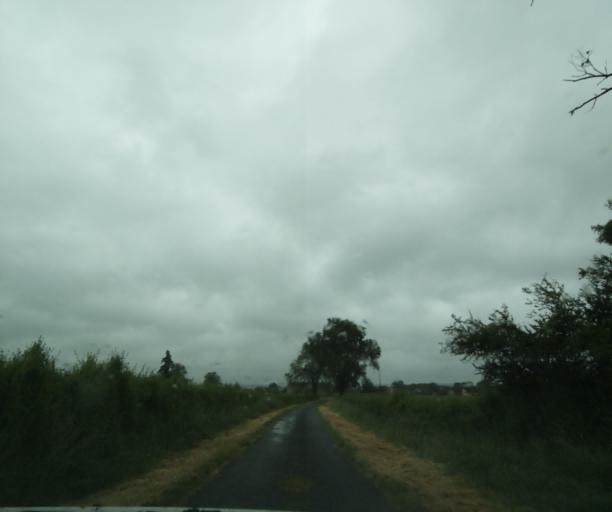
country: FR
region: Bourgogne
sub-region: Departement de Saone-et-Loire
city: Palinges
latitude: 46.5552
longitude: 4.2349
